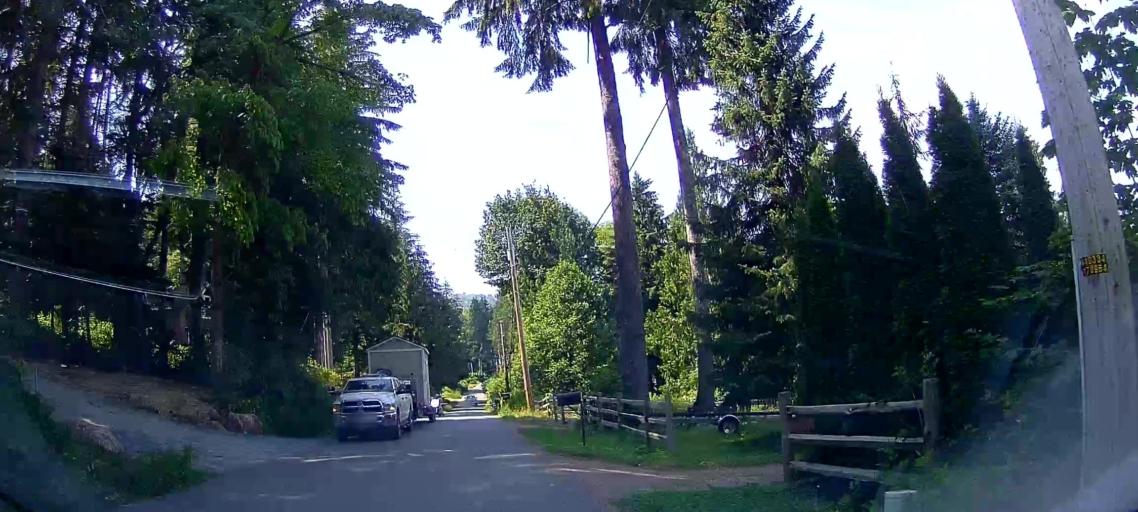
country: US
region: Washington
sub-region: Snohomish County
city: Arlington Heights
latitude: 48.3189
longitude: -122.0282
